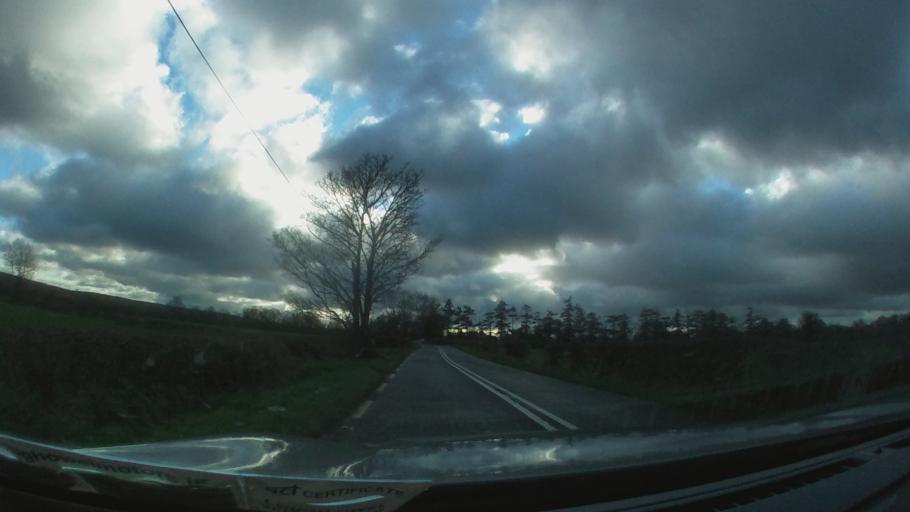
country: IE
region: Leinster
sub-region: Kilkenny
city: Thomastown
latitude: 52.5698
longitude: -7.1155
